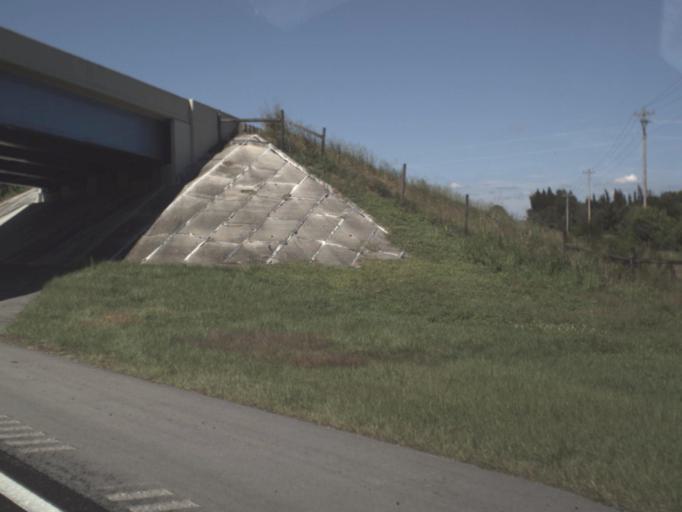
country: US
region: Florida
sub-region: Lee County
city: Suncoast Estates
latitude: 26.7397
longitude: -81.8504
